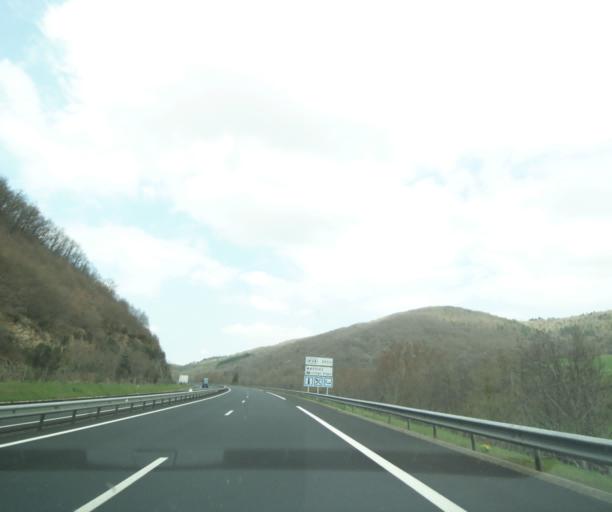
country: FR
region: Auvergne
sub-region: Departement du Cantal
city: Massiac
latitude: 45.2328
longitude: 3.2071
